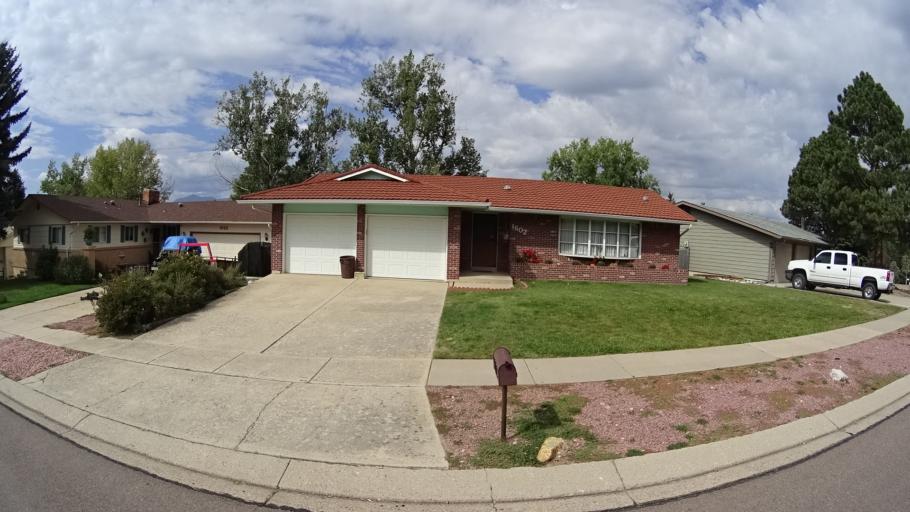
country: US
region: Colorado
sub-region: El Paso County
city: Cimarron Hills
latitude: 38.8555
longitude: -104.7315
